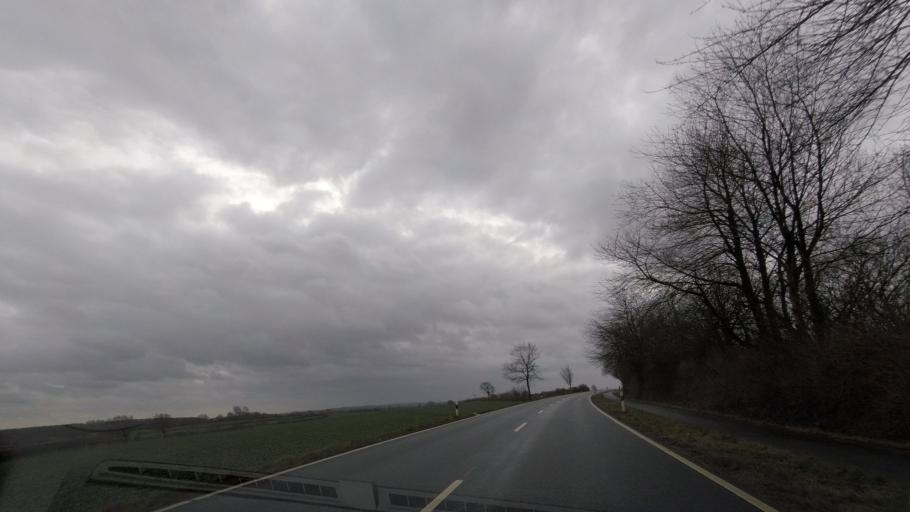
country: DE
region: Schleswig-Holstein
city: Tolk
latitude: 54.5692
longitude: 9.6451
